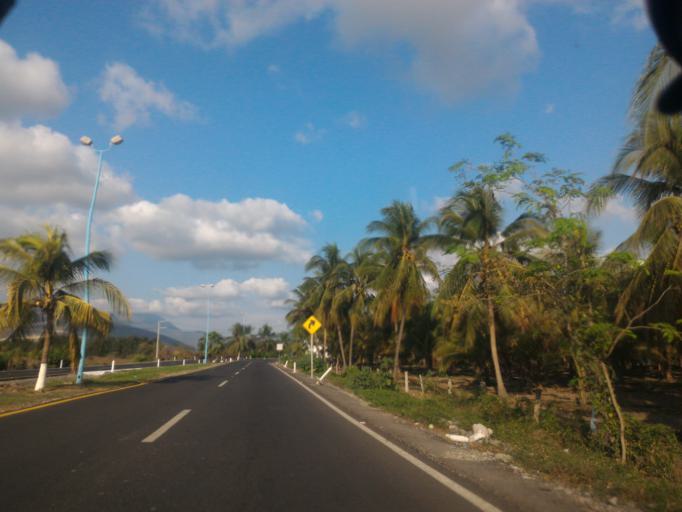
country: MX
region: Colima
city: Tecoman
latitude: 18.9426
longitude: -103.8900
